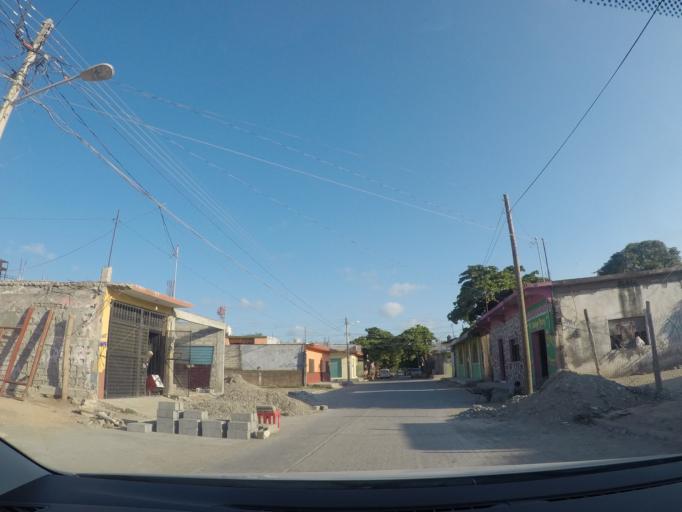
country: MX
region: Oaxaca
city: Juchitan de Zaragoza
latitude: 16.4362
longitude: -95.0290
